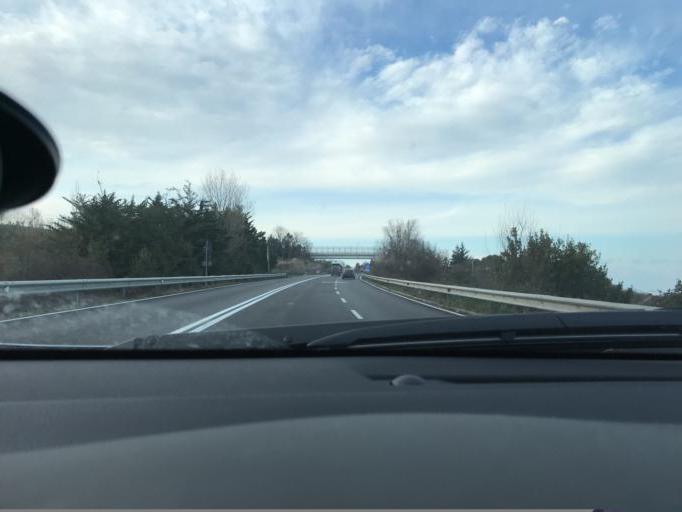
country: IT
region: The Marches
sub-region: Provincia di Ancona
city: Posatora
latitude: 43.5977
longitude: 13.4382
